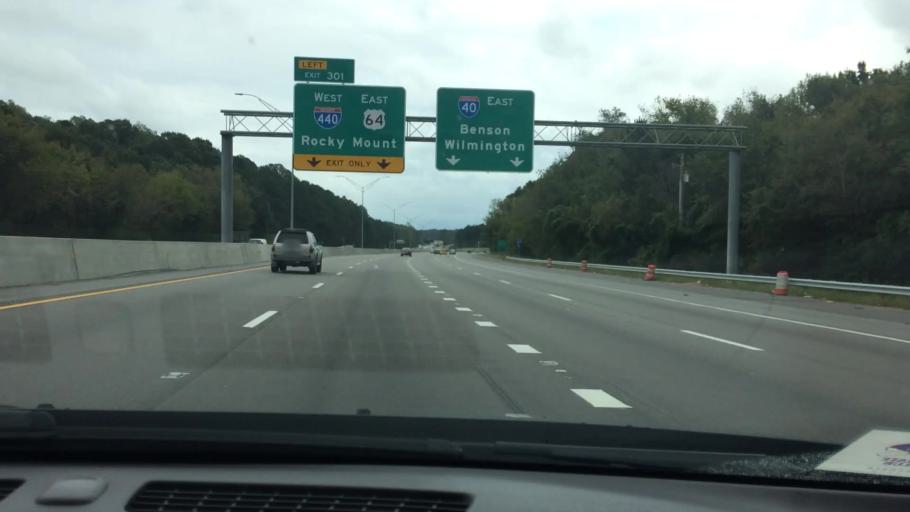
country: US
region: North Carolina
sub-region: Wake County
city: Raleigh
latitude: 35.7575
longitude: -78.6069
